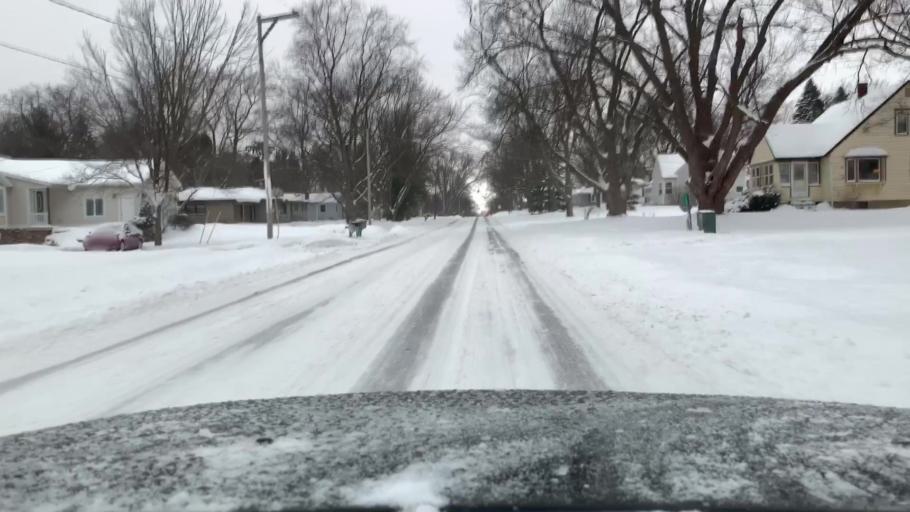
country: US
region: Michigan
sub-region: Ottawa County
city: Zeeland
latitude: 42.8000
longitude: -86.0383
